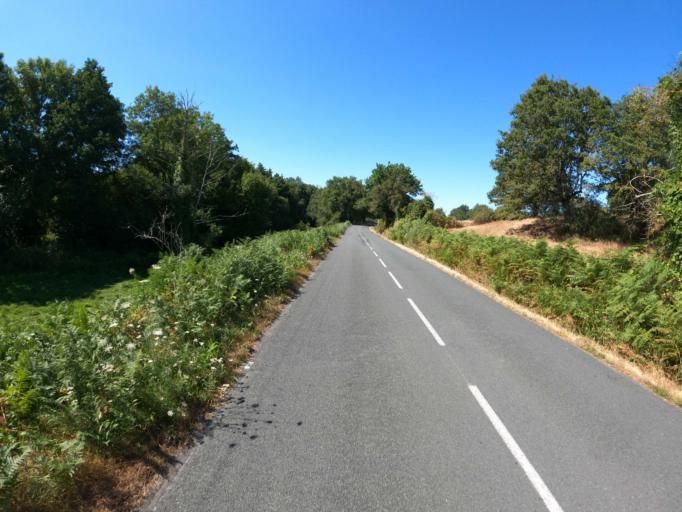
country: FR
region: Pays de la Loire
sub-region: Departement de la Vendee
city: Saint-Aubin-des-Ormeaux
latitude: 46.9790
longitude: -1.0517
